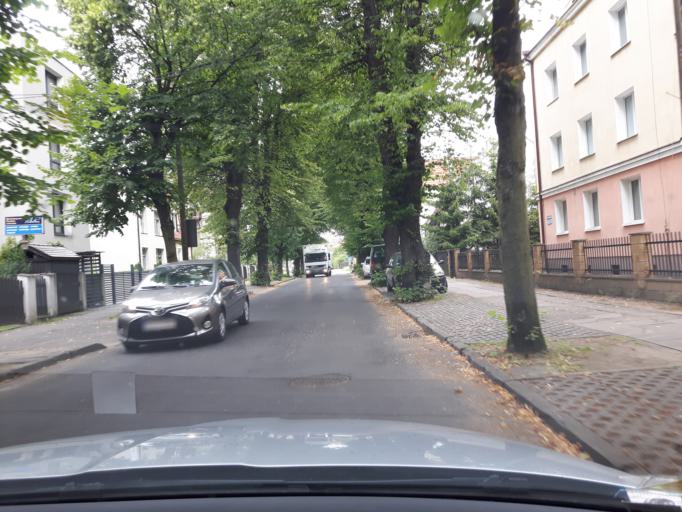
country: PL
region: Pomeranian Voivodeship
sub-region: Sopot
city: Sopot
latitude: 54.4124
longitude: 18.5765
